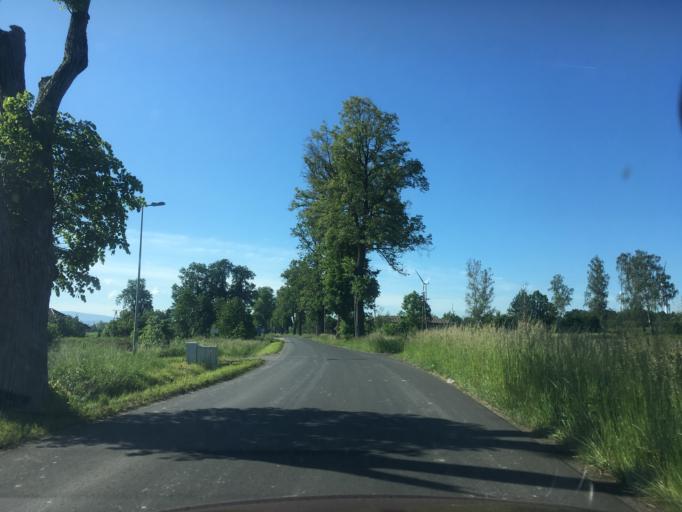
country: PL
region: Lower Silesian Voivodeship
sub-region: Powiat zgorzelecki
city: Sulikow
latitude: 51.1030
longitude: 15.0370
